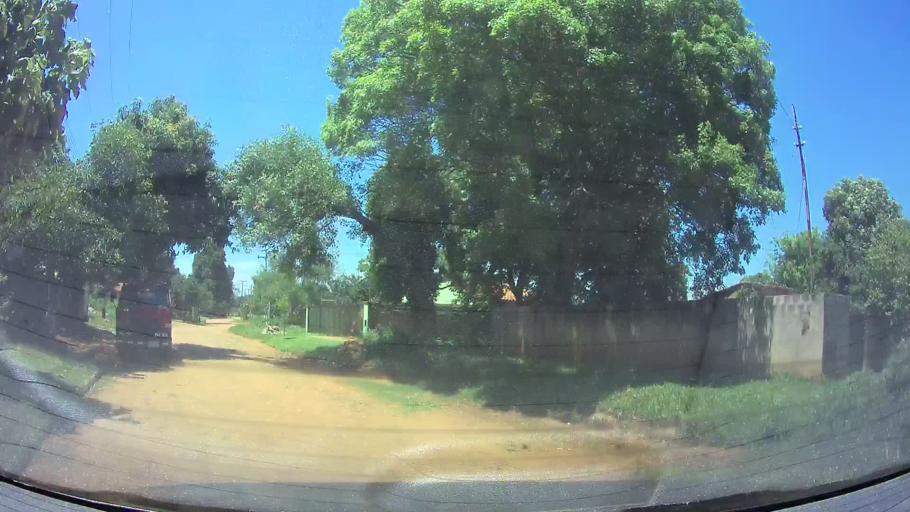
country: PY
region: Central
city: Limpio
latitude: -25.2423
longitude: -57.4875
